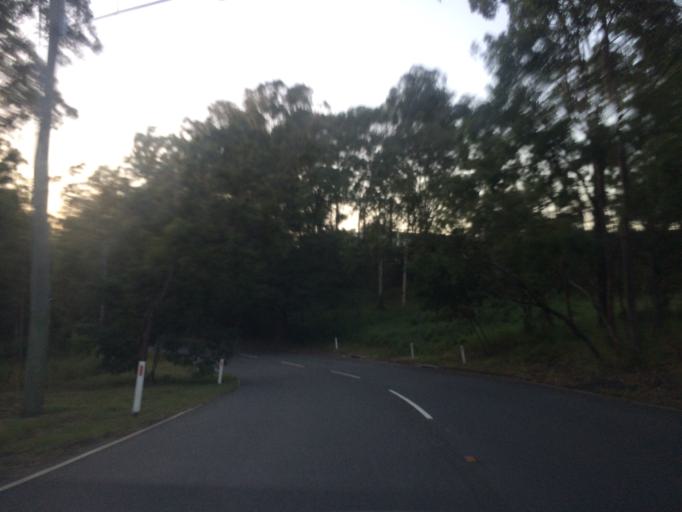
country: AU
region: Queensland
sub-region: Brisbane
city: Taringa
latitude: -27.4933
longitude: 152.9562
